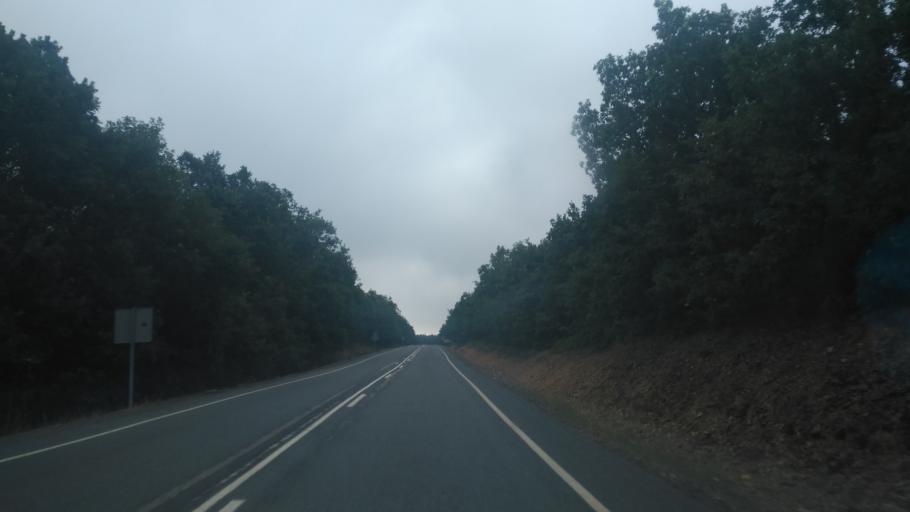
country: ES
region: Castille and Leon
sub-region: Provincia de Salamanca
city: Cilleros de la Bastida
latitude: 40.5653
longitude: -6.0714
